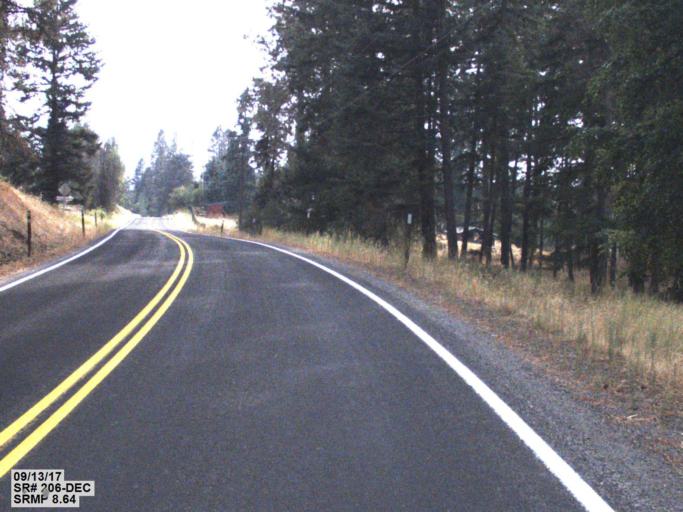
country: US
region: Washington
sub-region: Spokane County
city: Trentwood
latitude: 47.8263
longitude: -117.2094
